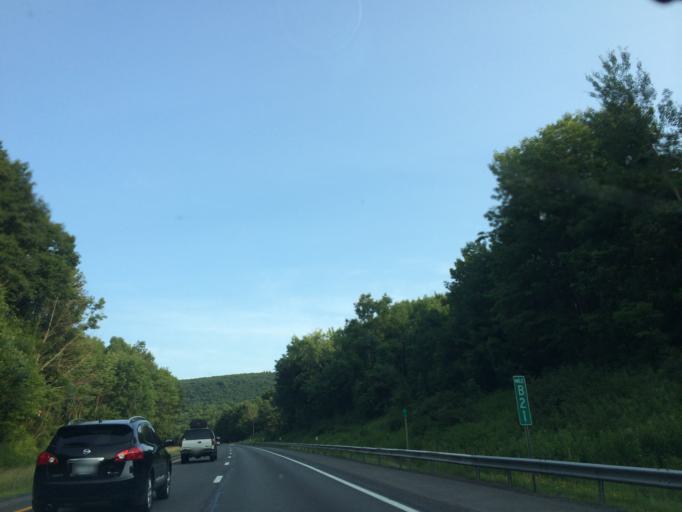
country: US
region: Massachusetts
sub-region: Berkshire County
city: Richmond
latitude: 42.3735
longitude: -73.4615
